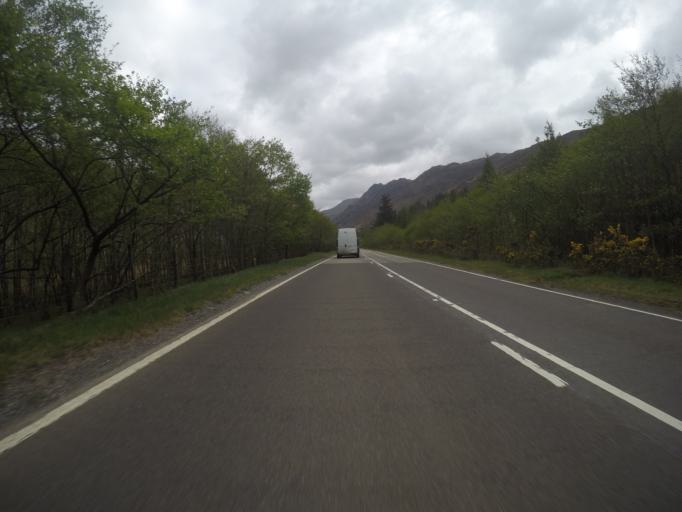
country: GB
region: Scotland
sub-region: Highland
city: Fort William
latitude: 57.2048
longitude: -5.3948
